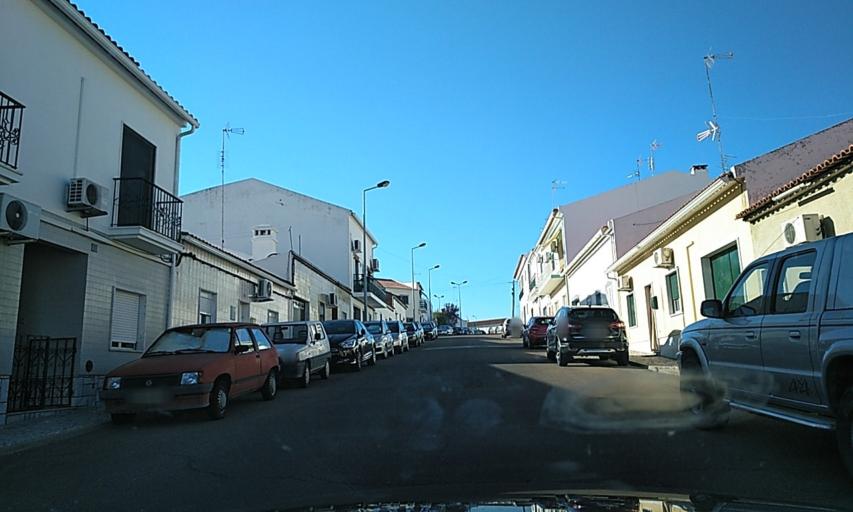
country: PT
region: Portalegre
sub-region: Campo Maior
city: Campo Maior
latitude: 39.0118
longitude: -7.0646
